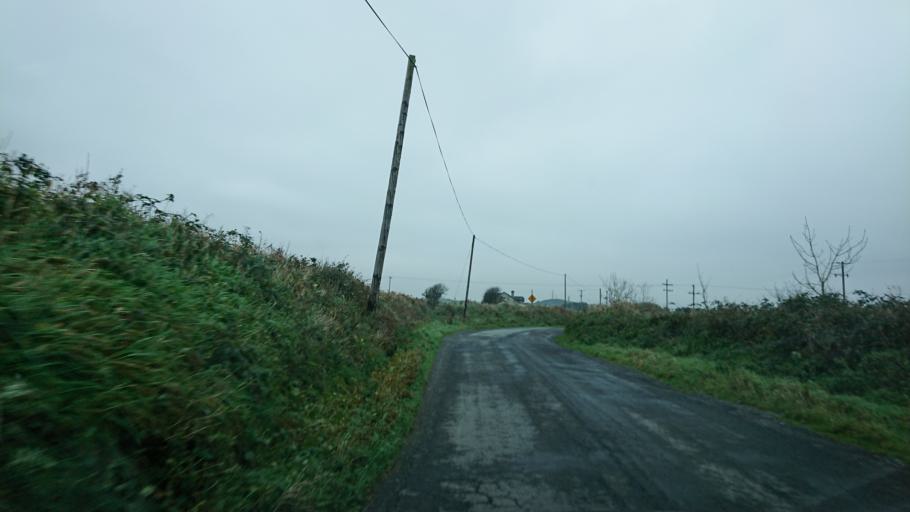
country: IE
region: Munster
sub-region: Waterford
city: Dunmore East
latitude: 52.1709
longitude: -7.0190
